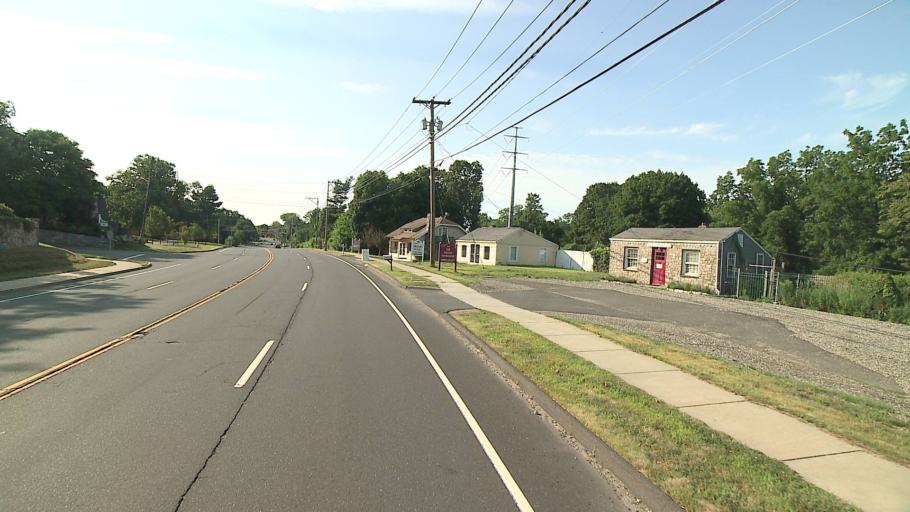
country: US
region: Connecticut
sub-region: Fairfield County
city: Wilton
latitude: 41.1925
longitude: -73.4292
